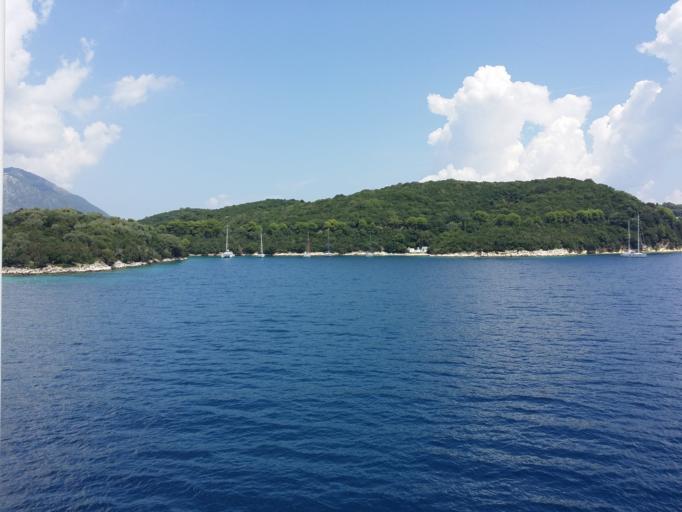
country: GR
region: Ionian Islands
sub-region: Lefkada
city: Nidri
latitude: 38.6845
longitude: 20.7407
